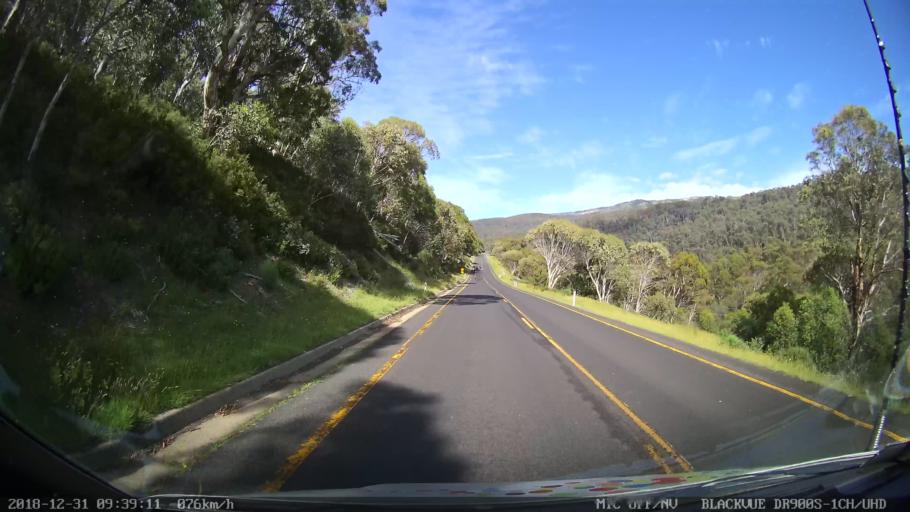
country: AU
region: New South Wales
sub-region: Snowy River
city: Jindabyne
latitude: -36.4784
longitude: 148.3584
